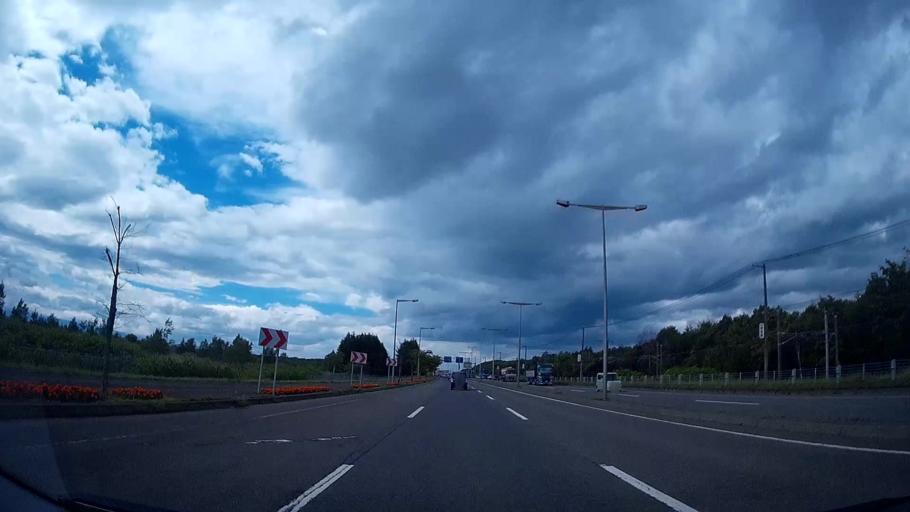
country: JP
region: Hokkaido
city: Chitose
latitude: 42.8133
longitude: 141.6686
